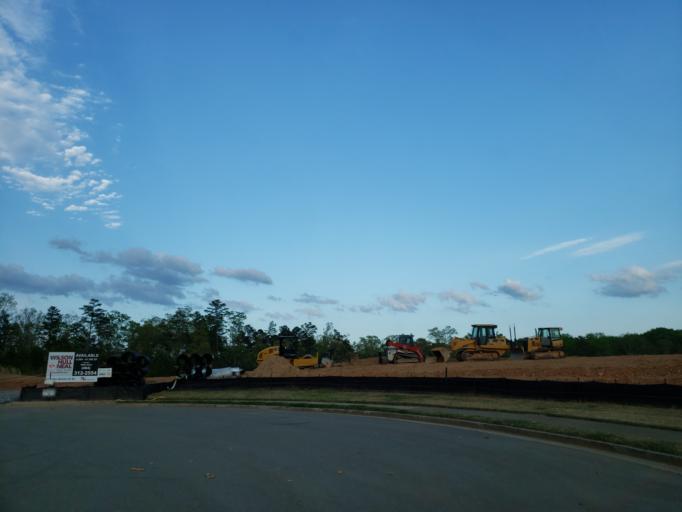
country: US
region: Georgia
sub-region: Cherokee County
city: Canton
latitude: 34.2848
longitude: -84.4640
